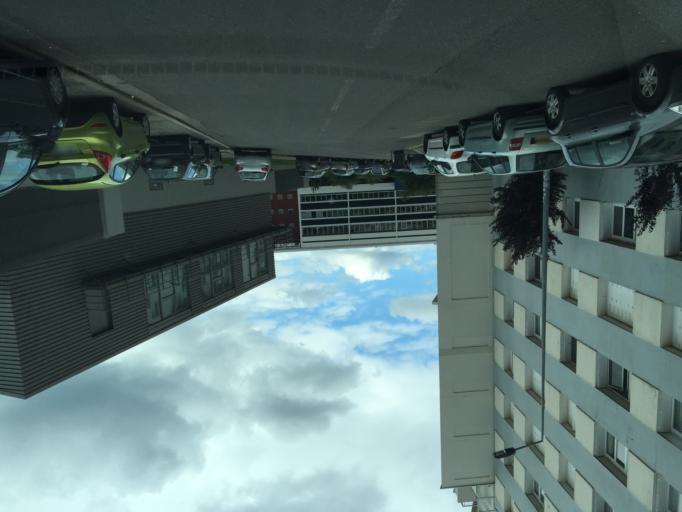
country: FR
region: Rhone-Alpes
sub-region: Departement de la Loire
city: Saint-Etienne
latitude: 45.4274
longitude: 4.3931
